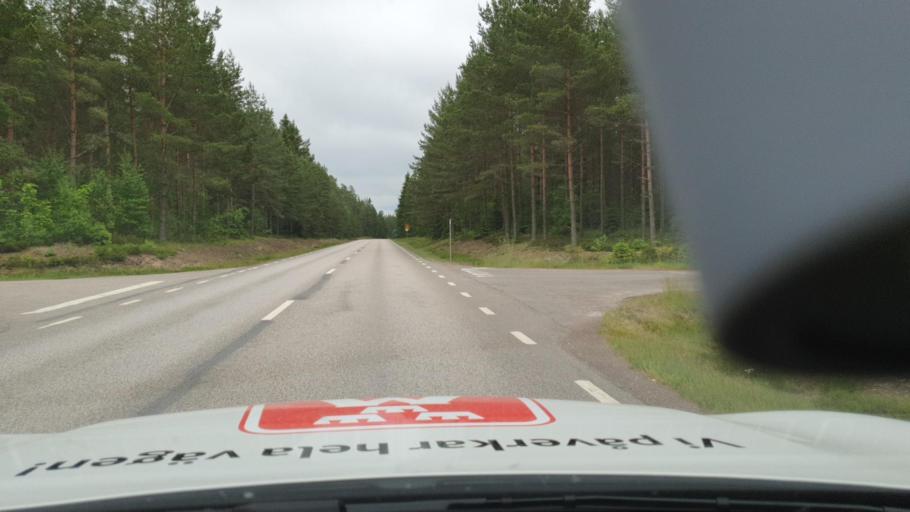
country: SE
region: Vaestra Goetaland
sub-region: Hjo Kommun
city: Hjo
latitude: 58.3465
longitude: 14.2240
